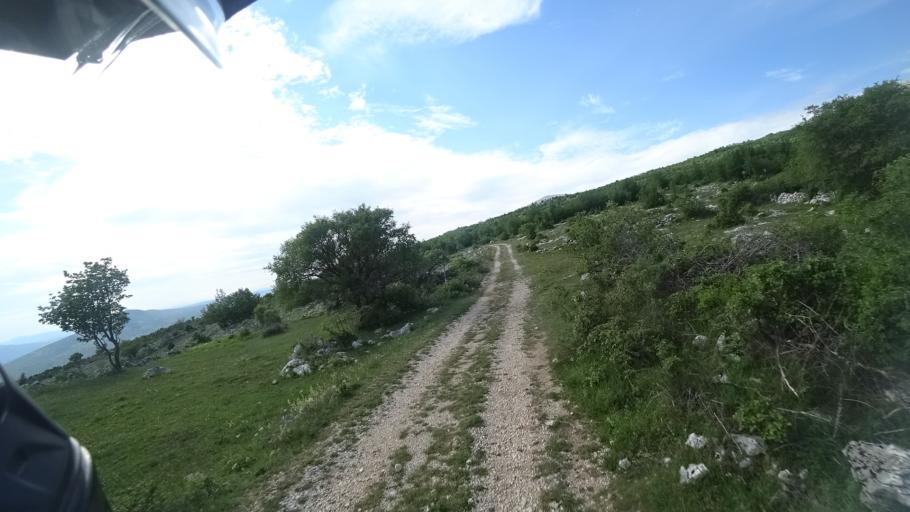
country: HR
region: Splitsko-Dalmatinska
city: Hrvace
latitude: 43.7807
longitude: 16.4429
